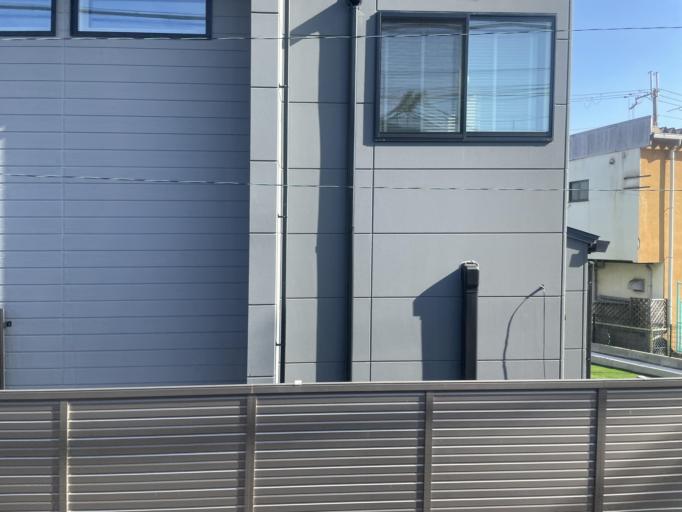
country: JP
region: Osaka
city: Kashihara
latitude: 34.5395
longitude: 135.6845
